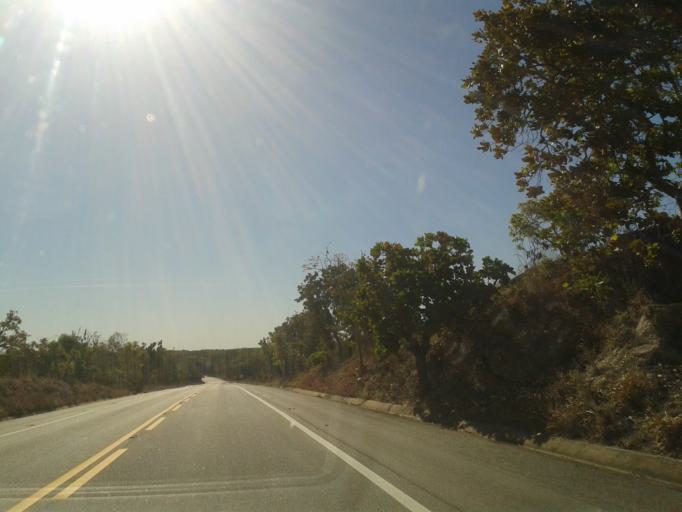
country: BR
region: Goias
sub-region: Itapuranga
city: Itapuranga
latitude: -15.4893
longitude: -50.3231
